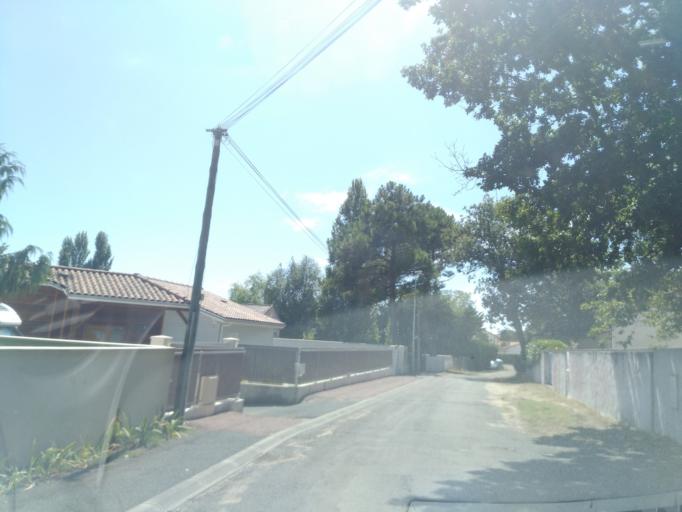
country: FR
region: Poitou-Charentes
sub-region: Departement de la Charente-Maritime
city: Saint-Palais-sur-Mer
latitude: 45.6594
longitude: -1.0772
